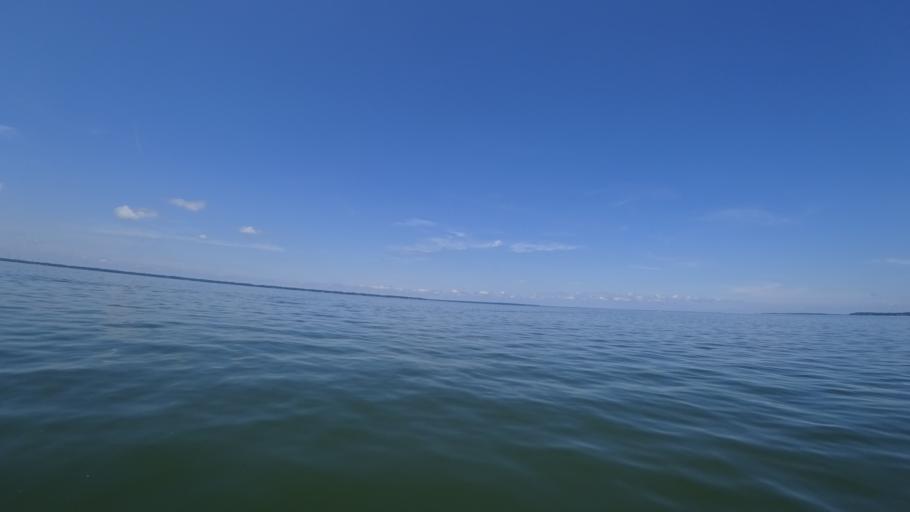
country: US
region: Virginia
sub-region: City of Newport News
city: Newport News
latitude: 37.0063
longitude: -76.4785
